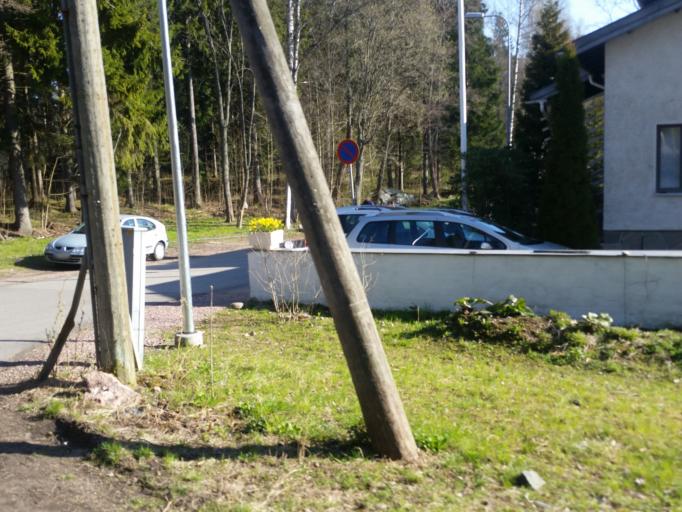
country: FI
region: Uusimaa
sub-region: Helsinki
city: Teekkarikylae
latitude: 60.1548
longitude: 24.8590
